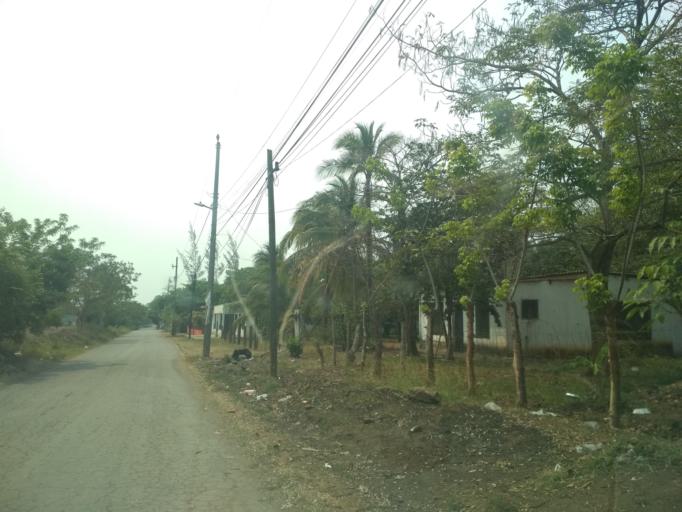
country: MX
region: Veracruz
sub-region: Veracruz
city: Delfino Victoria (Santa Fe)
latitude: 19.2040
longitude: -96.2692
